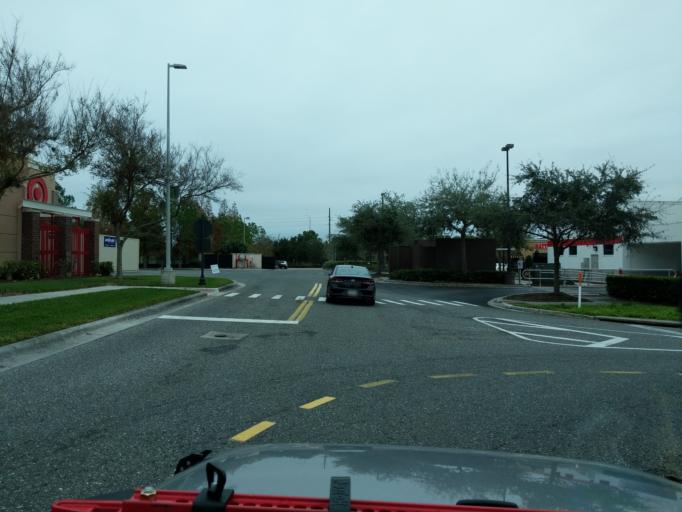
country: US
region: Florida
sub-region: Orange County
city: Winter Garden
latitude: 28.5204
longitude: -81.5861
